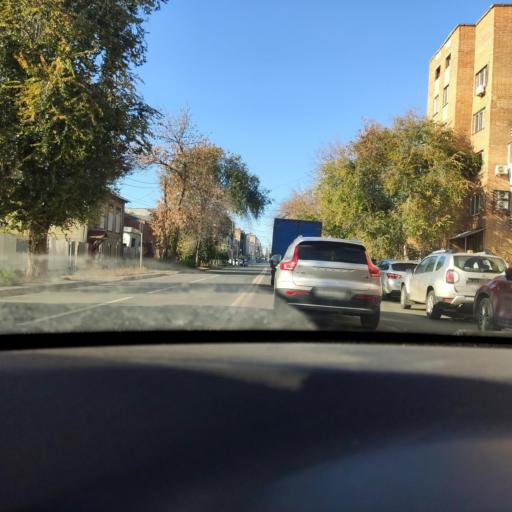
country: RU
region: Samara
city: Samara
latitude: 53.1830
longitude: 50.0980
